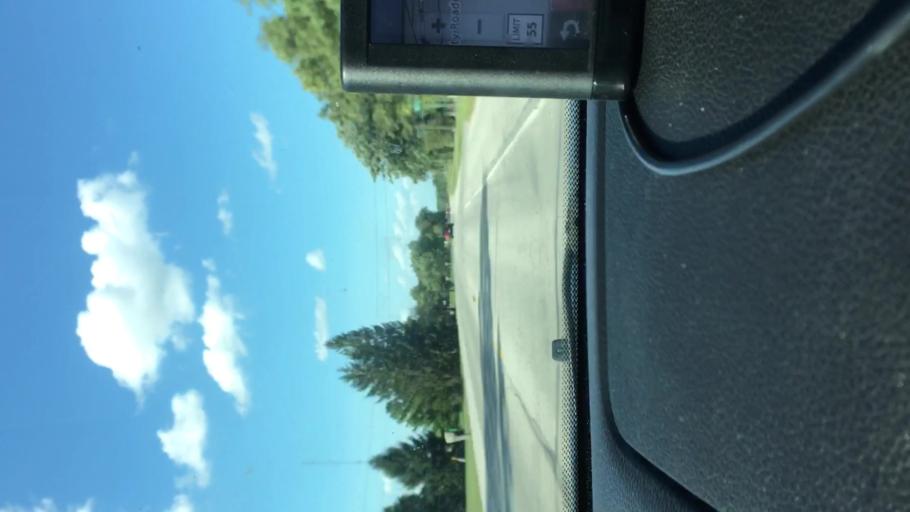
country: US
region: Indiana
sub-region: Jay County
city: Portland
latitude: 40.3945
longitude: -84.9779
